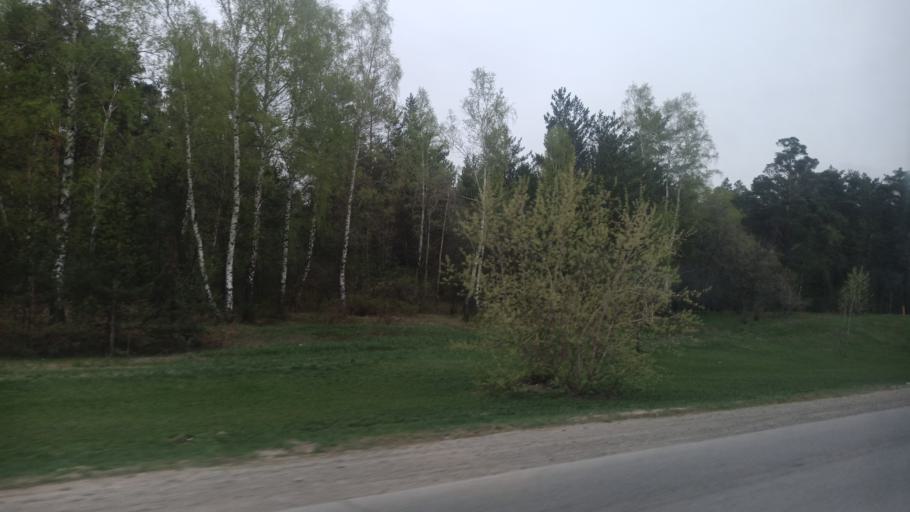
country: RU
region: Altai Krai
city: Yuzhnyy
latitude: 53.2614
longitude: 83.7017
